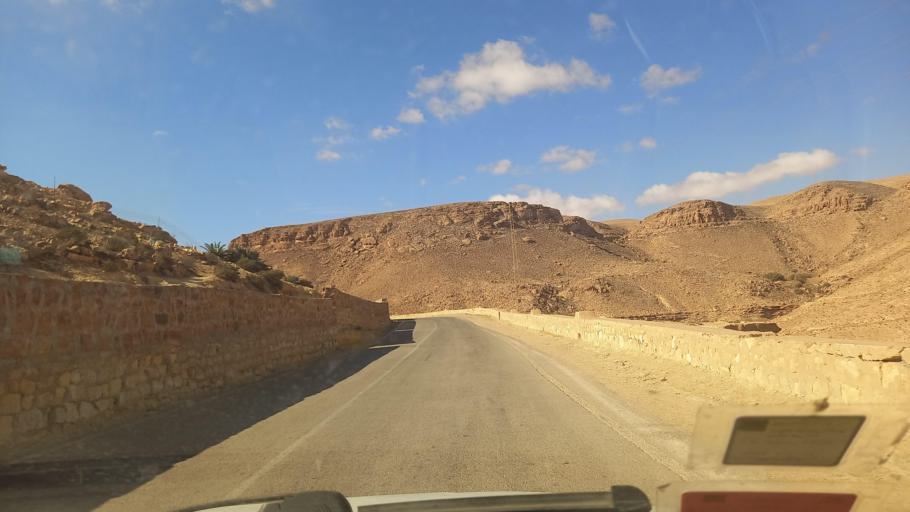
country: TN
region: Tataouine
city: Tataouine
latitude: 32.9138
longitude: 10.2600
